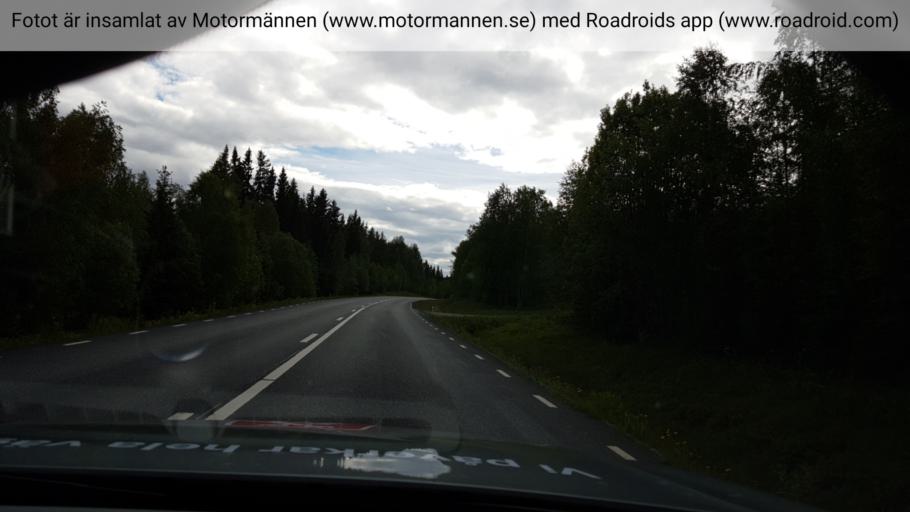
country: SE
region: Jaemtland
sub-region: Stroemsunds Kommun
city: Stroemsund
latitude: 64.1067
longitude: 15.5985
